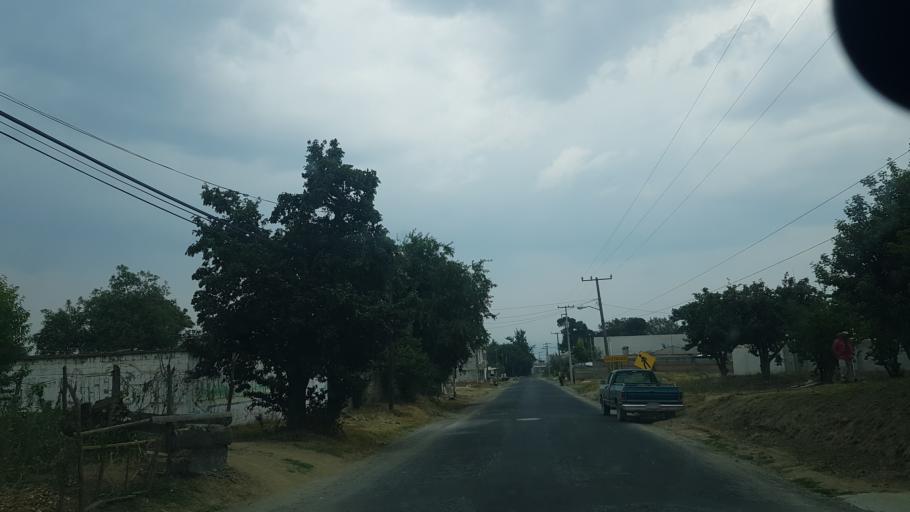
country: MX
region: Puebla
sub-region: Chiautzingo
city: San Nicolas Zecalacoayan
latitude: 19.1768
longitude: -98.4907
